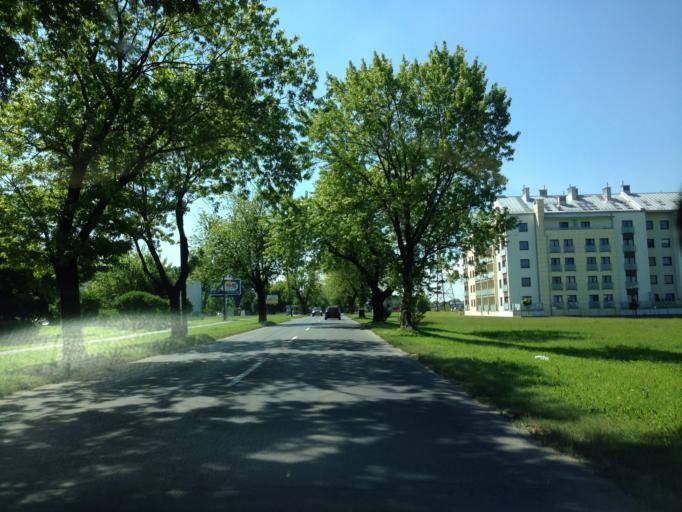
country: PL
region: Masovian Voivodeship
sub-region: Warszawa
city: Bemowo
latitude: 52.2336
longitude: 20.8967
